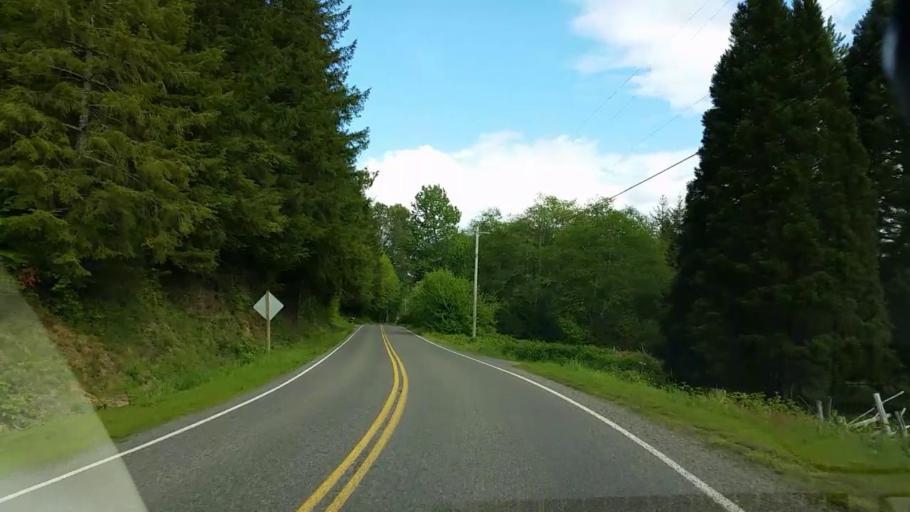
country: US
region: Washington
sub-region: Mason County
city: Shelton
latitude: 47.3202
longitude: -123.2683
